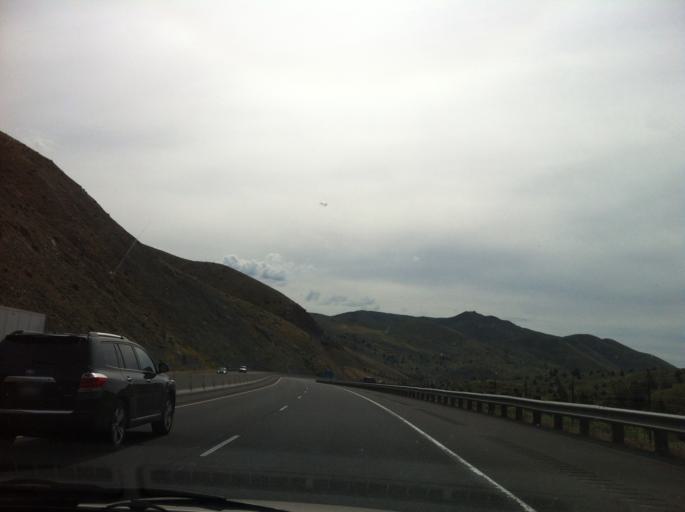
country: US
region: Idaho
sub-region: Washington County
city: Weiser
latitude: 44.5224
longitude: -117.3896
